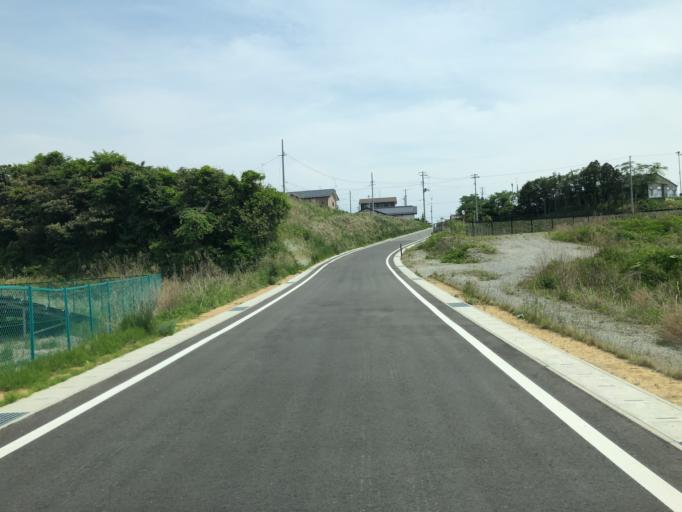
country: JP
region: Miyagi
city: Marumori
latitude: 37.8275
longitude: 140.9558
